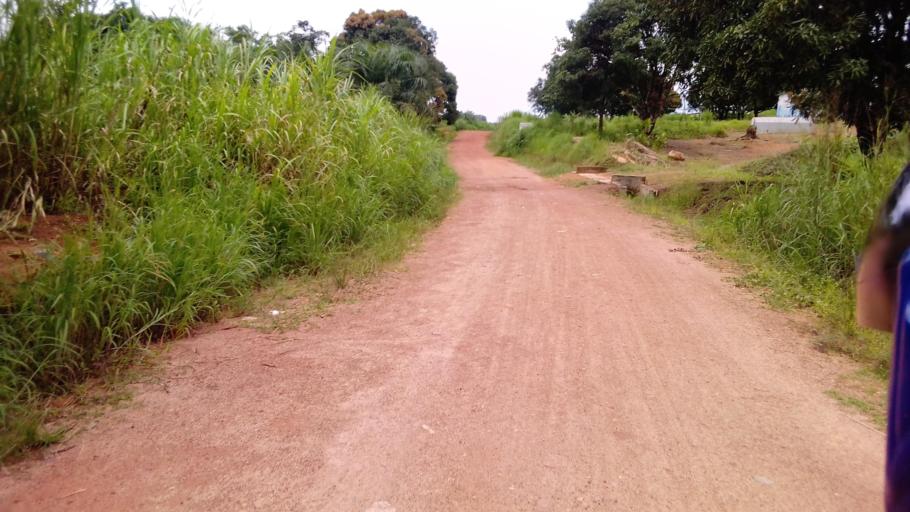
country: SL
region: Eastern Province
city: Koidu
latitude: 8.6617
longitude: -10.9413
